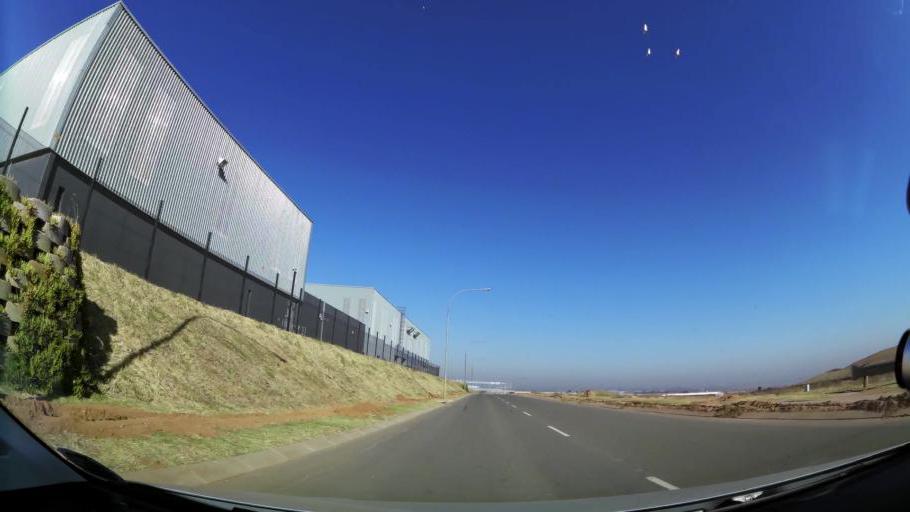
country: ZA
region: Gauteng
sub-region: City of Johannesburg Metropolitan Municipality
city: Modderfontein
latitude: -26.0468
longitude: 28.1692
